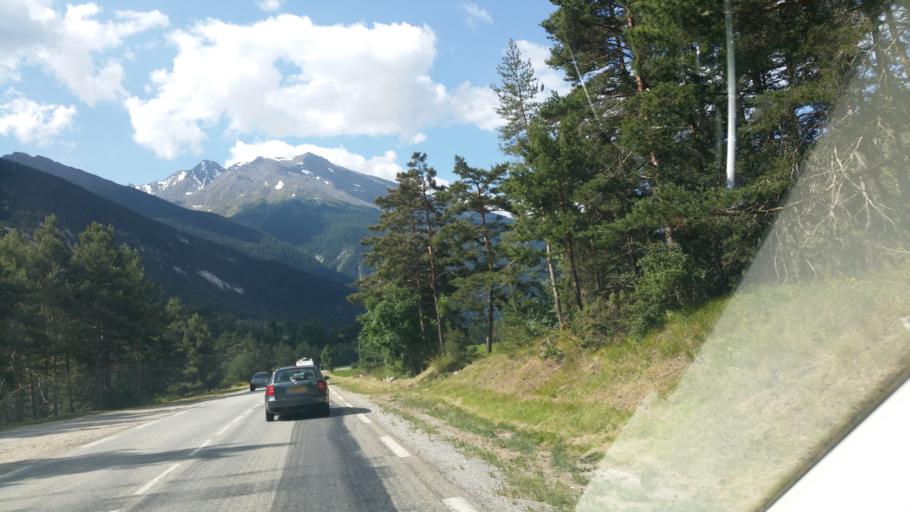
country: FR
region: Rhone-Alpes
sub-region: Departement de la Savoie
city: Modane
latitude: 45.2484
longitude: 6.7975
